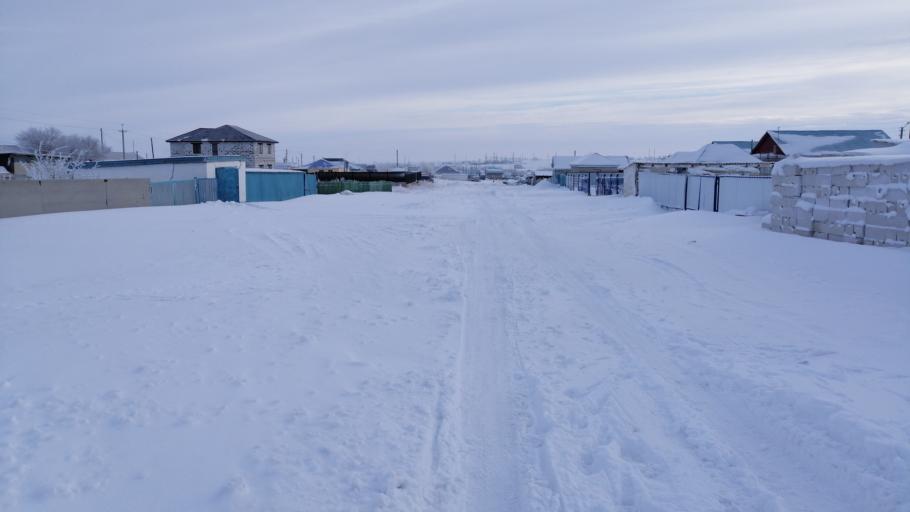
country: KZ
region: Aqtoebe
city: Aqtobe
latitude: 50.2467
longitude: 56.8486
